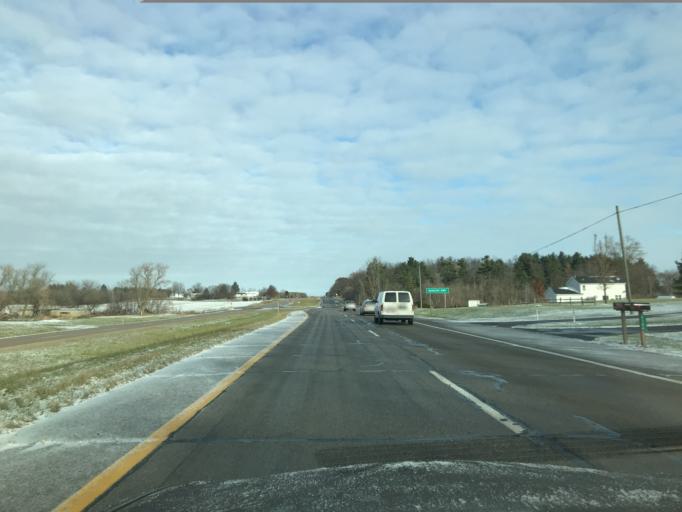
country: US
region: Michigan
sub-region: Eaton County
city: Dimondale
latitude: 42.6163
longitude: -84.6224
